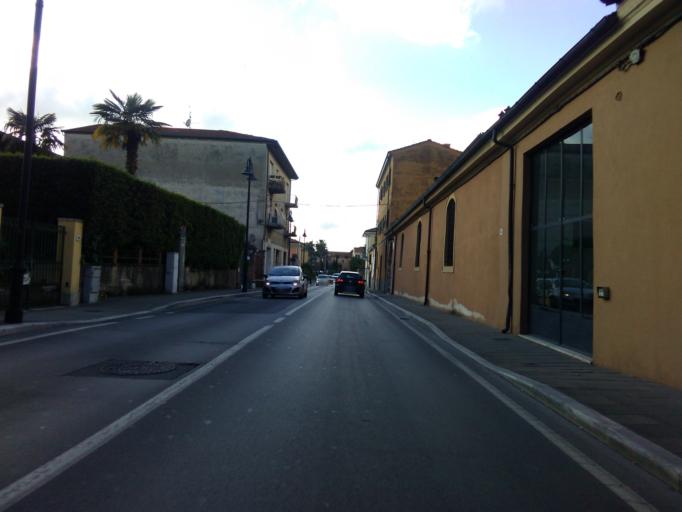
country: IT
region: Tuscany
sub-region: Provincia di Lucca
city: Pietrasanta
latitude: 43.9571
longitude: 10.2302
